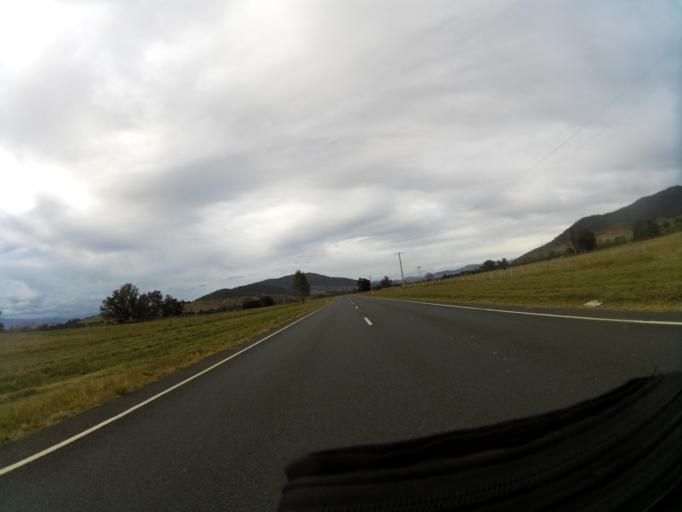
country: AU
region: New South Wales
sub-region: Snowy River
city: Jindabyne
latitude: -36.1106
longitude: 147.9792
